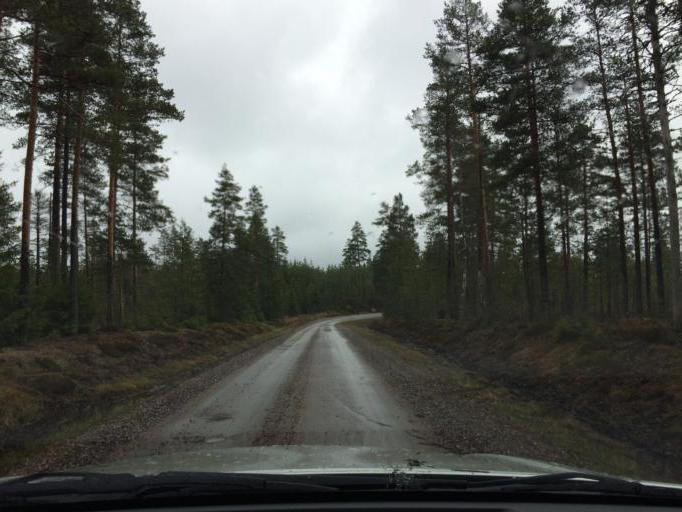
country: SE
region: OErebro
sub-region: Hallefors Kommun
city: Haellefors
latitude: 60.0283
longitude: 14.5560
